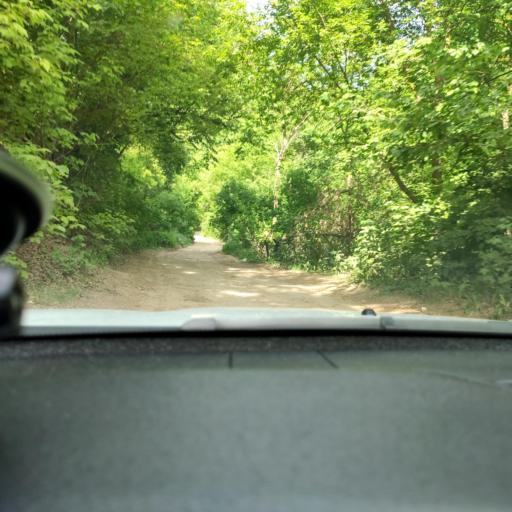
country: RU
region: Samara
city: Volzhskiy
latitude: 53.3373
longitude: 50.2027
